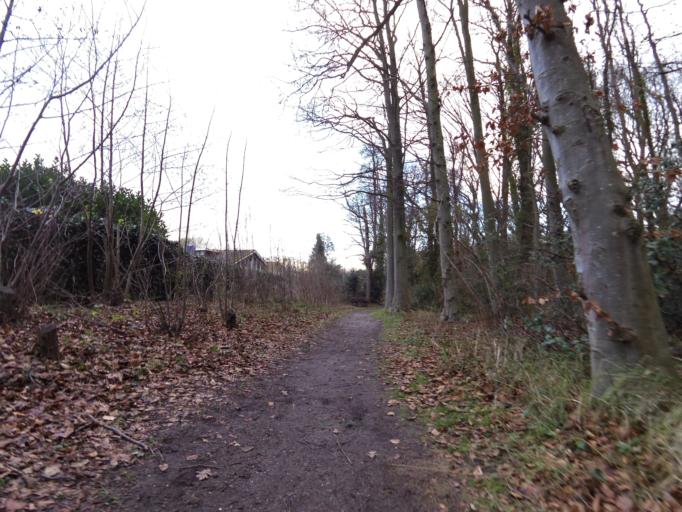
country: NL
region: South Holland
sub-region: Gemeente Brielle
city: Brielle
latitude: 51.9151
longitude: 4.0918
